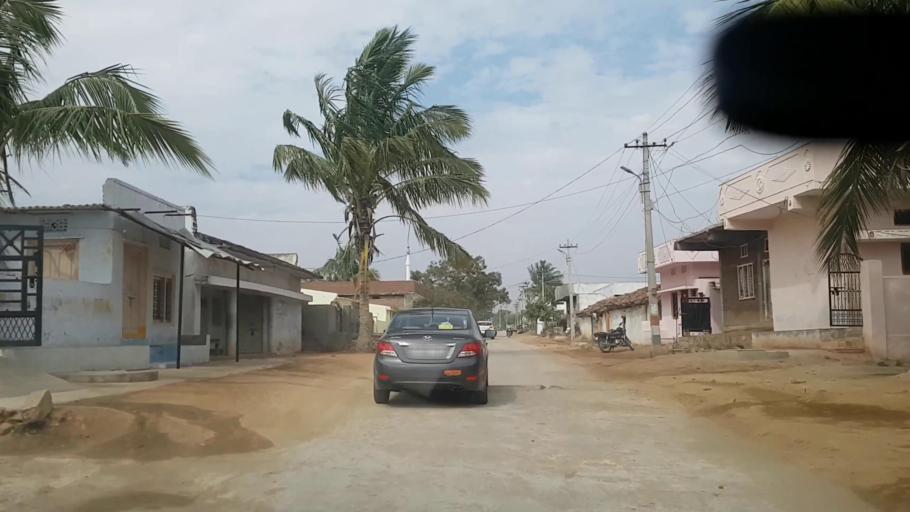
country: IN
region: Telangana
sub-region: Rangareddi
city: Lal Bahadur Nagar
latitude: 17.1686
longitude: 78.7834
